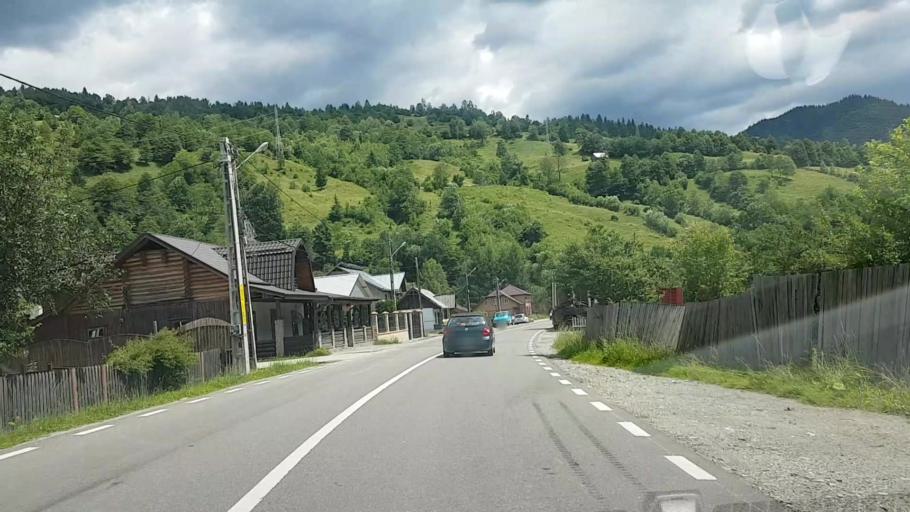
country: RO
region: Suceava
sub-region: Comuna Brosteni
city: Brosteni
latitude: 47.2609
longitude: 25.6850
